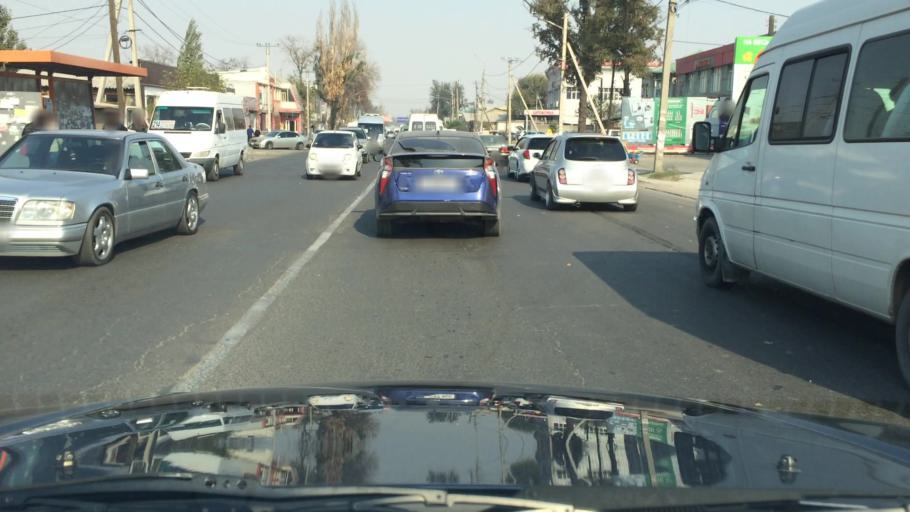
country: KG
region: Chuy
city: Lebedinovka
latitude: 42.8784
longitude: 74.6377
